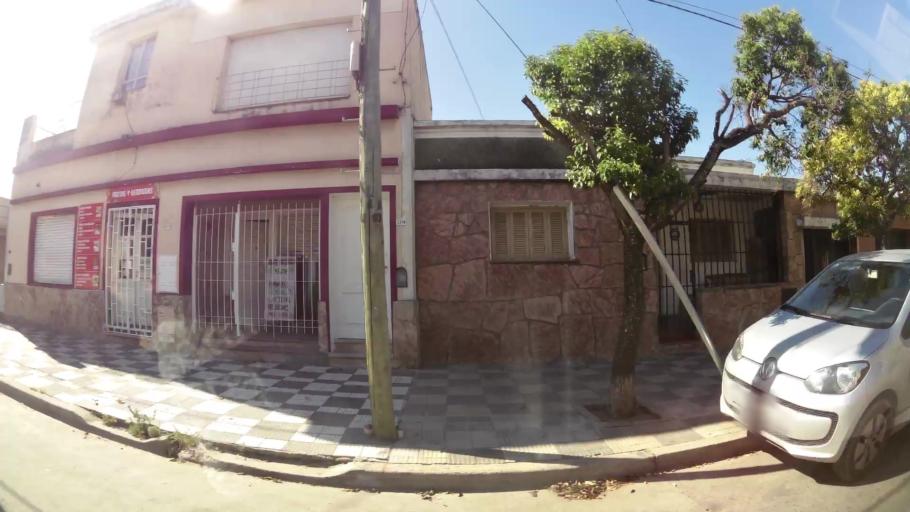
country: AR
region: Cordoba
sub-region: Departamento de Capital
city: Cordoba
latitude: -31.4152
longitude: -64.1508
